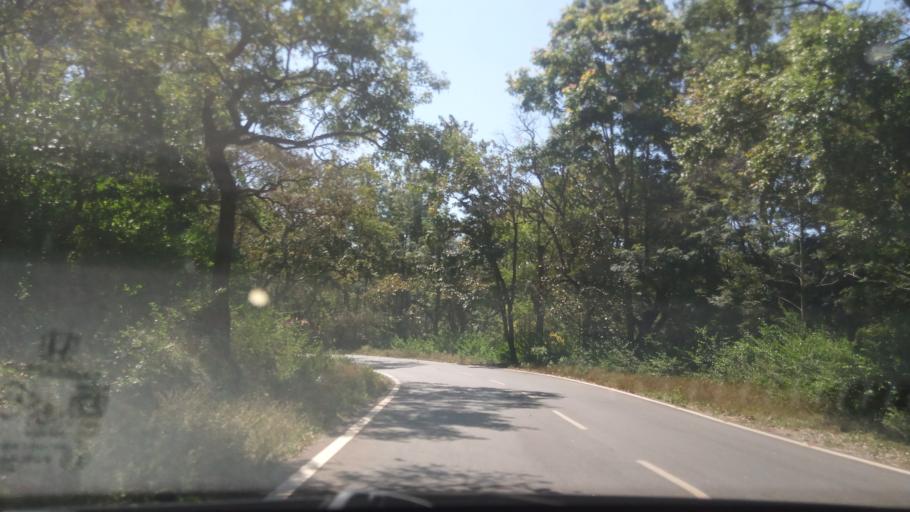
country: IN
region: Karnataka
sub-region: Chikmagalur
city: Chikmagalur
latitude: 13.4487
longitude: 75.8022
